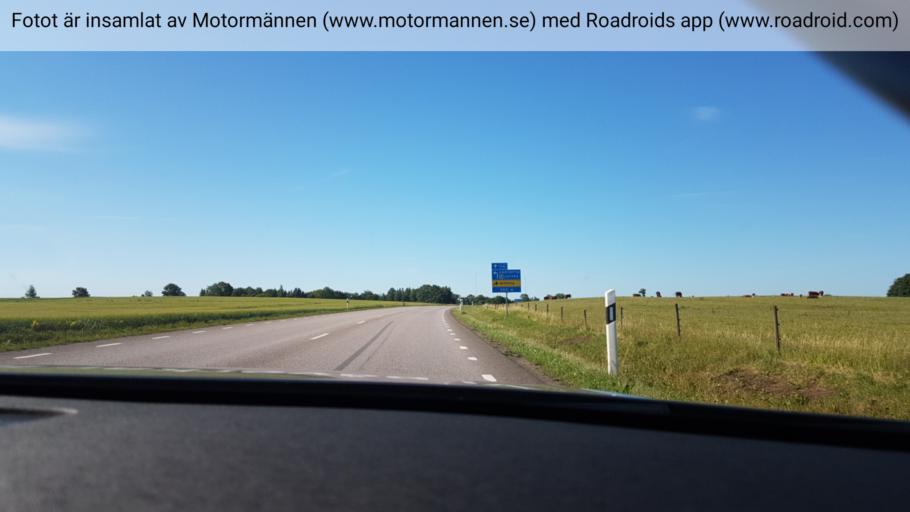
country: SE
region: Vaestra Goetaland
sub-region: Falkopings Kommun
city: Falkoeping
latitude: 58.1387
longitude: 13.5631
